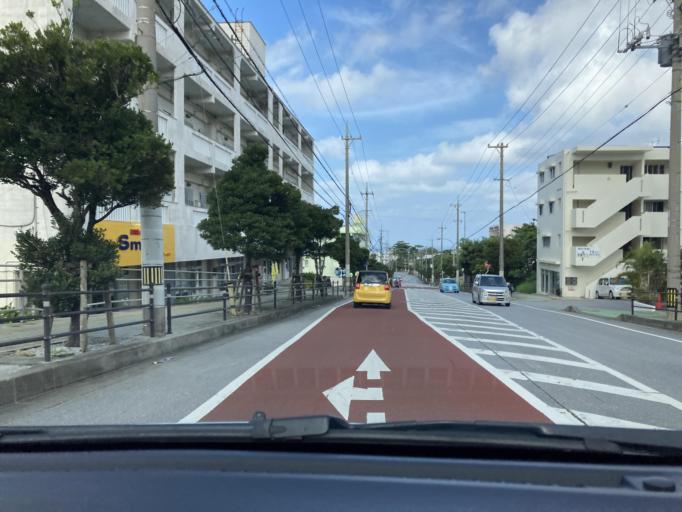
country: JP
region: Okinawa
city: Ginowan
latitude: 26.2618
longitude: 127.7513
